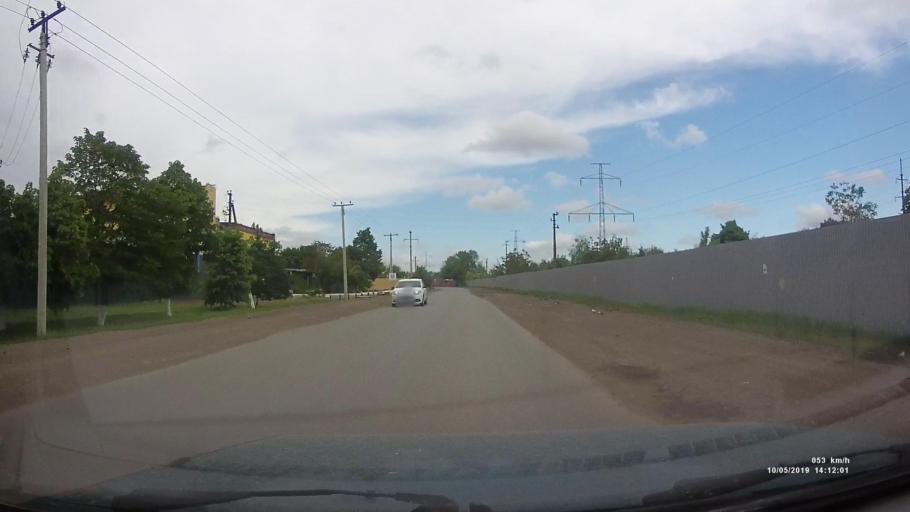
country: RU
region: Rostov
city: Azov
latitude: 47.0939
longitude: 39.4212
